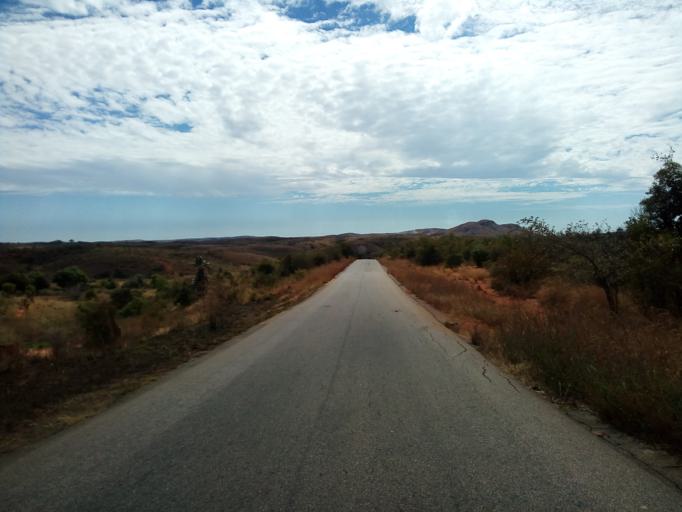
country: MG
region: Betsiboka
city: Maevatanana
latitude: -17.2483
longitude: 46.9268
